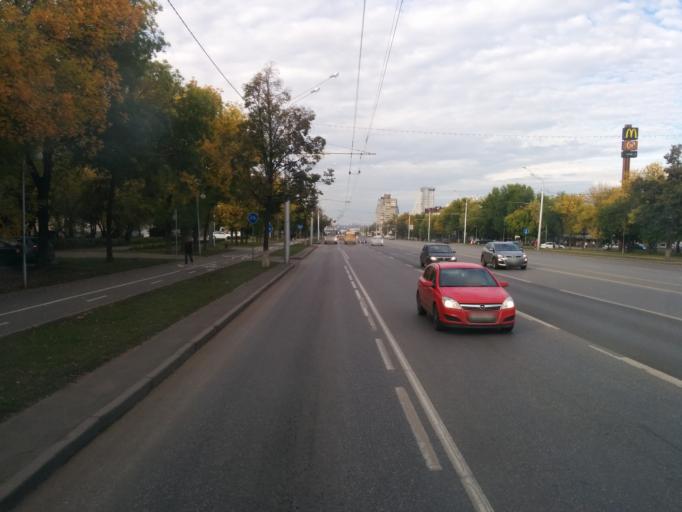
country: RU
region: Bashkortostan
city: Ufa
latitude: 54.7786
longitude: 56.0307
